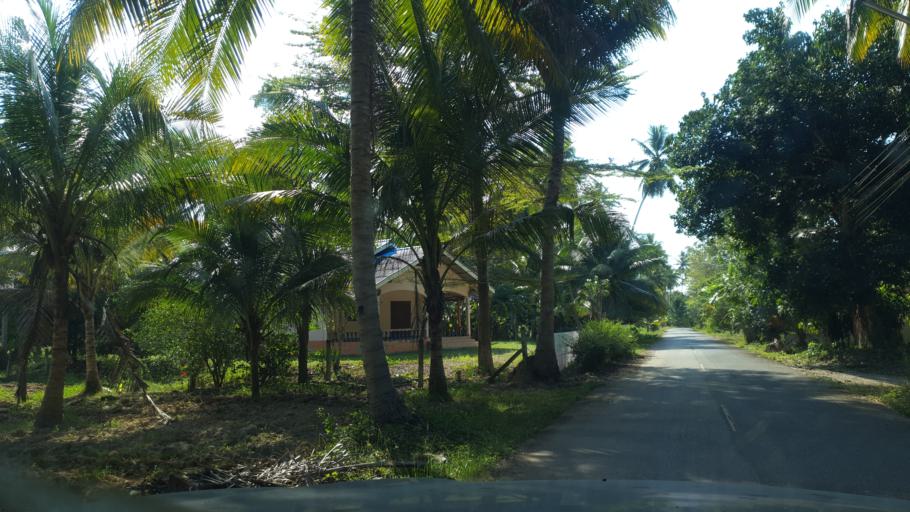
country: TH
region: Prachuap Khiri Khan
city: Thap Sakae
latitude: 11.3637
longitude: 99.5527
